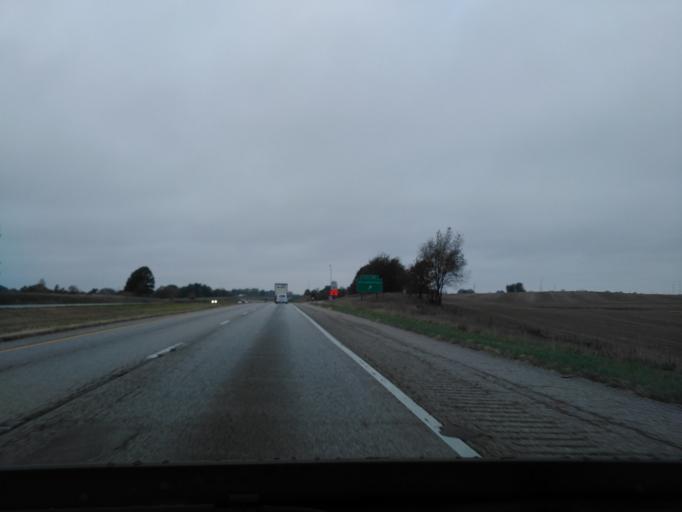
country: US
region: Illinois
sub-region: Bond County
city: Greenville
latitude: 38.8339
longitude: -89.5387
